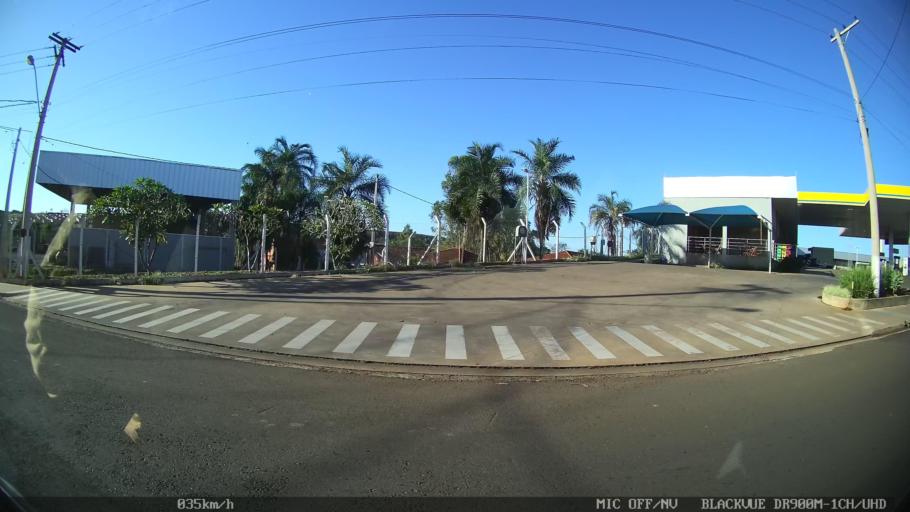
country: BR
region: Sao Paulo
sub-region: Guapiacu
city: Guapiacu
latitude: -20.7889
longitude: -49.2374
